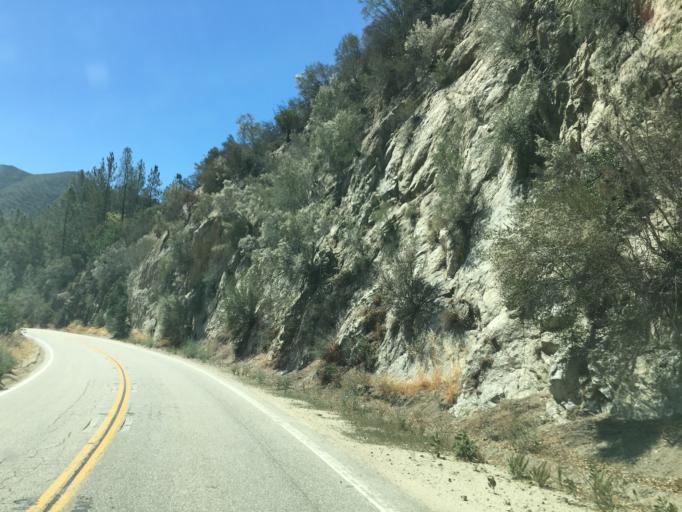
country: US
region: California
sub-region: Los Angeles County
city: Castaic
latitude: 34.6099
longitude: -118.5626
